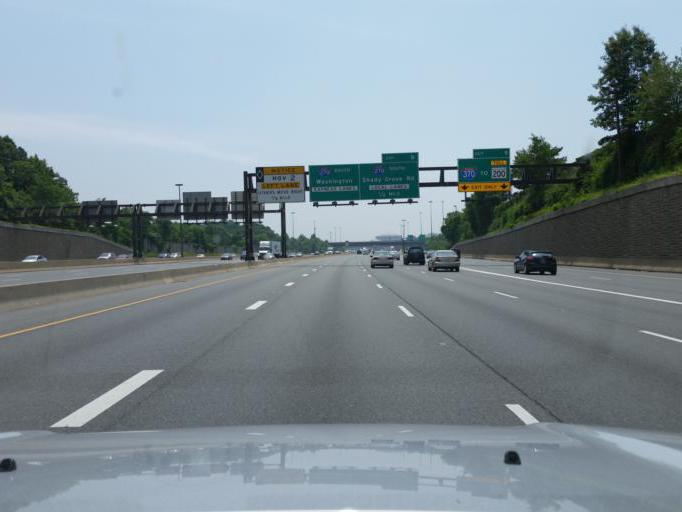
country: US
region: Maryland
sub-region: Montgomery County
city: Gaithersburg
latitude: 39.1275
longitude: -77.2030
